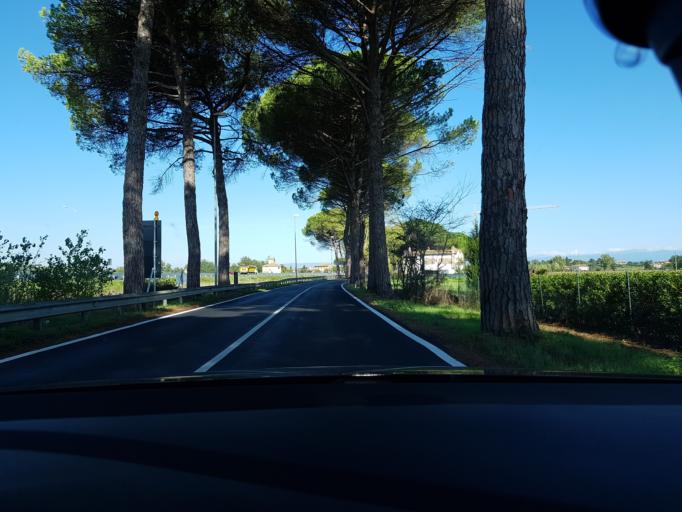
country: IT
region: Tuscany
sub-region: Province of Pisa
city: Ponte A Elsa
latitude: 43.6801
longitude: 10.9153
